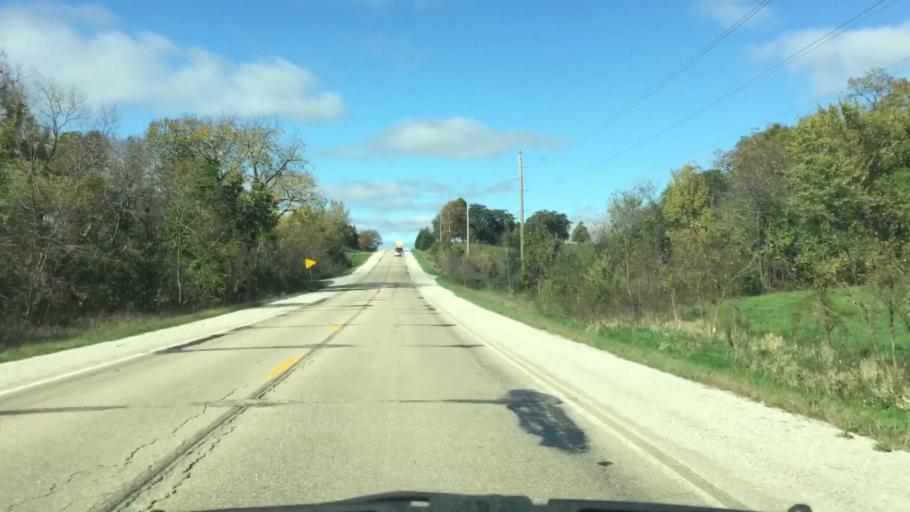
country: US
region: Iowa
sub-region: Decatur County
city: Leon
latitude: 40.7413
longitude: -93.7897
